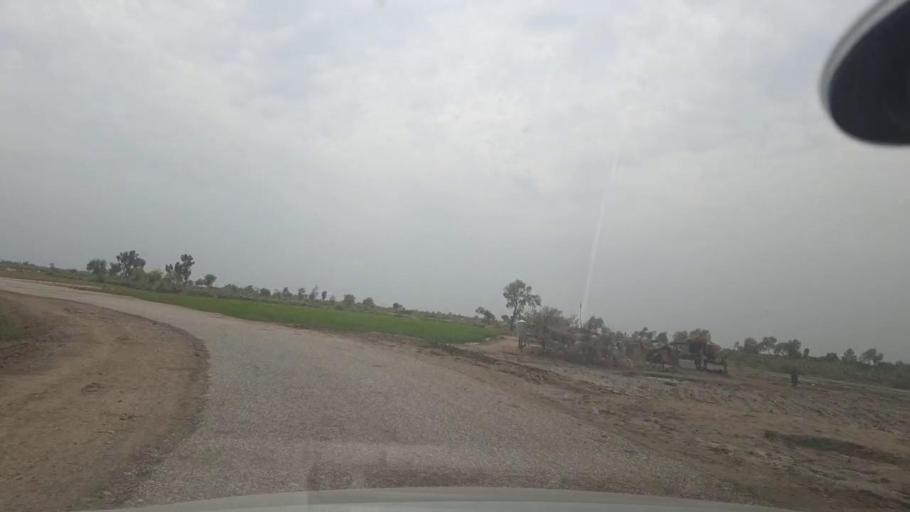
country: PK
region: Balochistan
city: Mehrabpur
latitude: 28.0539
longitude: 68.1361
